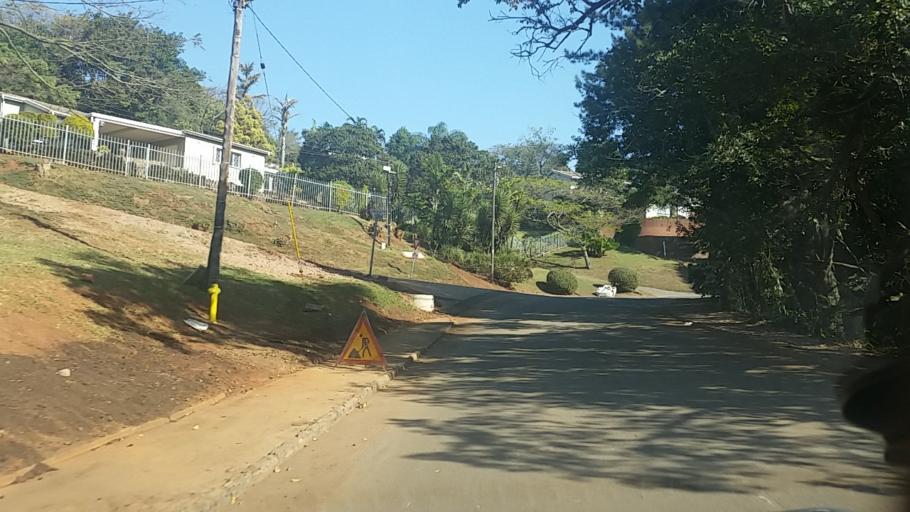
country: ZA
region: KwaZulu-Natal
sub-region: eThekwini Metropolitan Municipality
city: Berea
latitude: -29.8439
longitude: 30.9111
